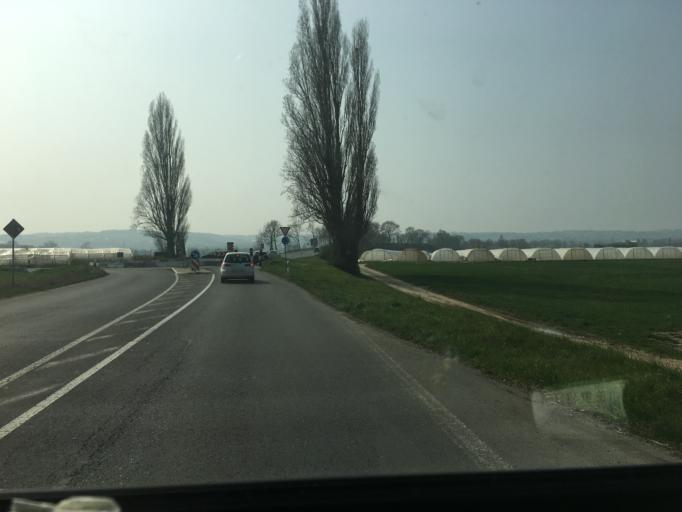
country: DE
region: North Rhine-Westphalia
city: Bornheim
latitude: 50.7792
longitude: 6.9904
